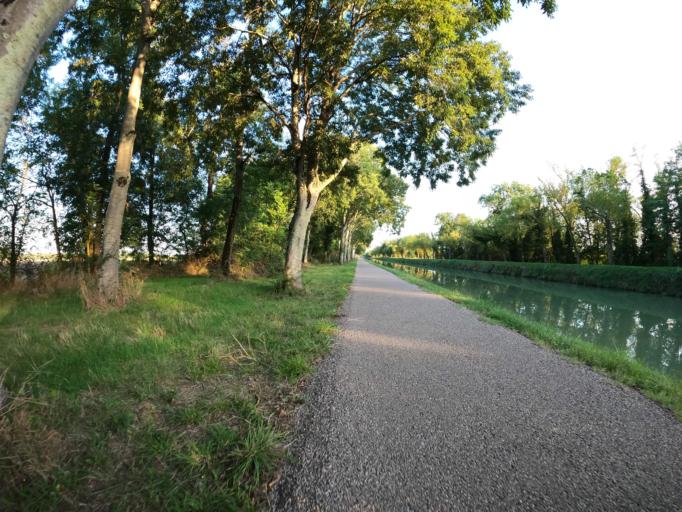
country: FR
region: Midi-Pyrenees
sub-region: Departement du Tarn-et-Garonne
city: Saint-Porquier
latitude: 44.0028
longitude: 1.1880
